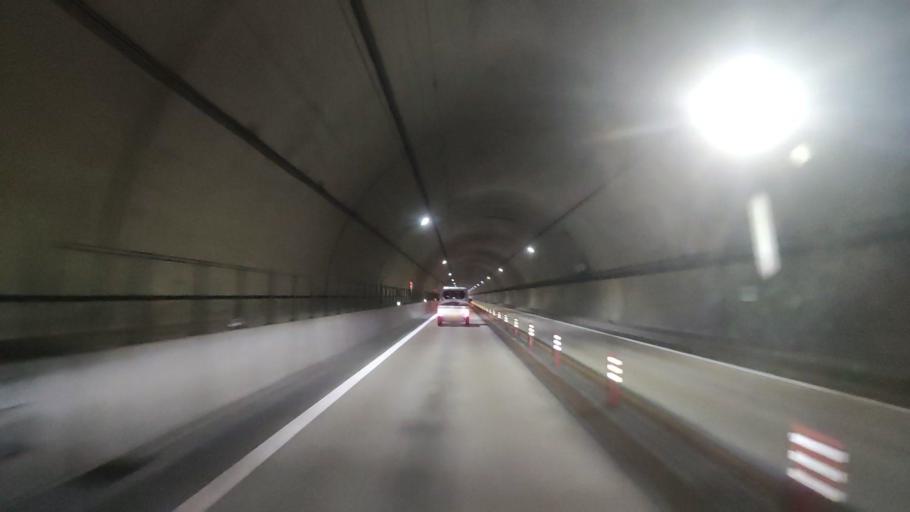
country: JP
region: Wakayama
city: Tanabe
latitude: 33.6235
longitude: 135.4184
